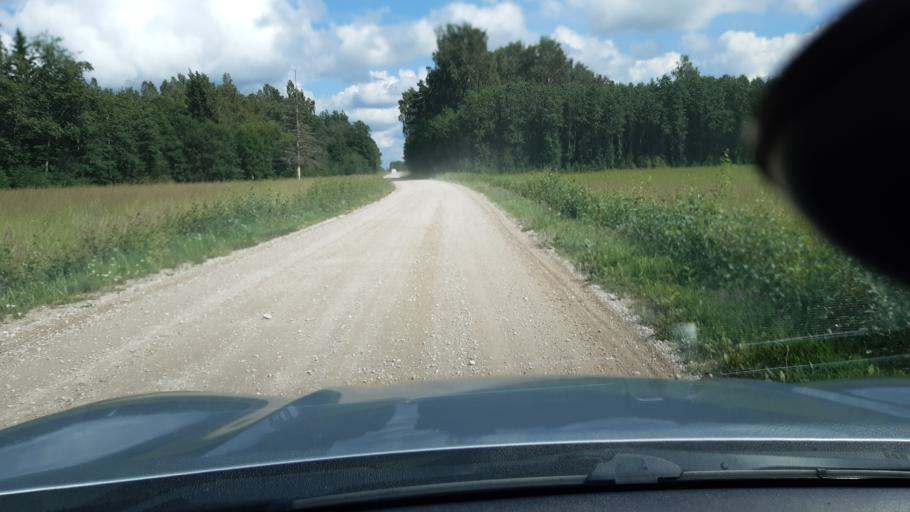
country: EE
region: Raplamaa
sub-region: Kehtna vald
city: Kehtna
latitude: 58.9106
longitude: 25.1486
